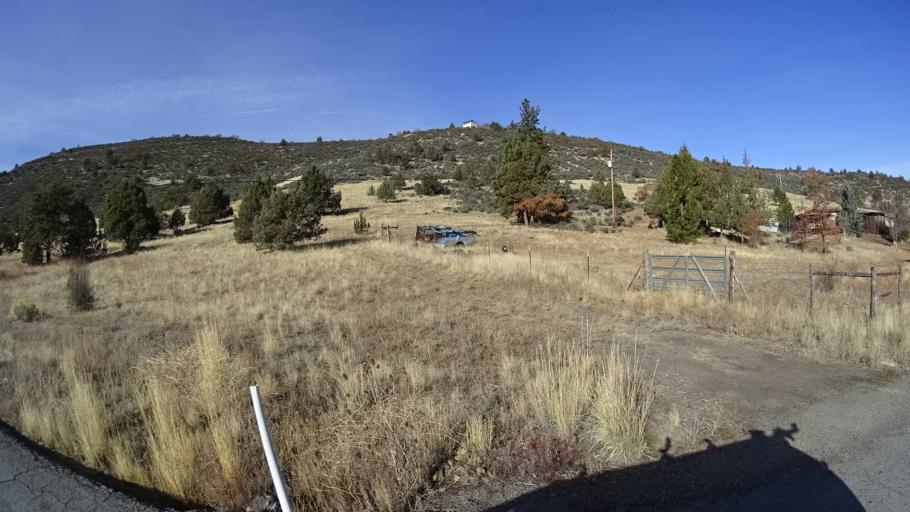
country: US
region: California
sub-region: Siskiyou County
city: Montague
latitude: 41.6257
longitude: -122.5734
